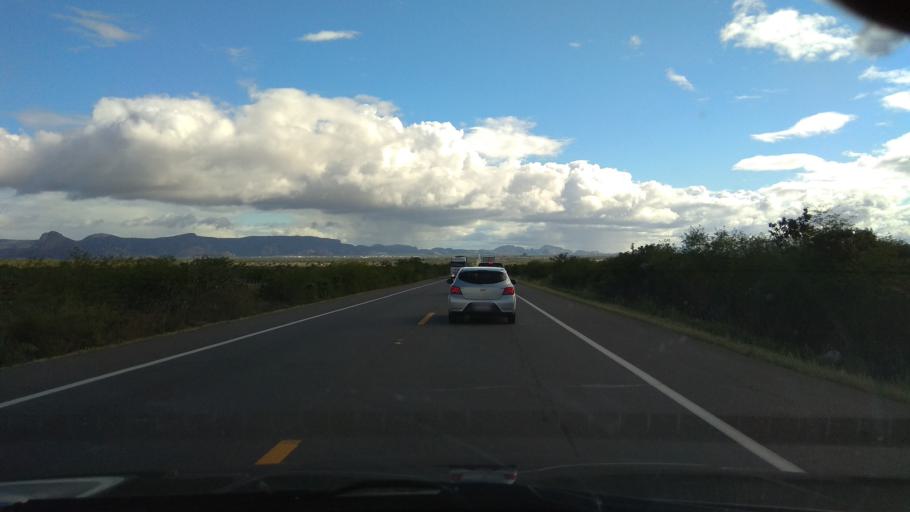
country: BR
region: Bahia
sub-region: Castro Alves
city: Castro Alves
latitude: -12.6609
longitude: -39.6302
